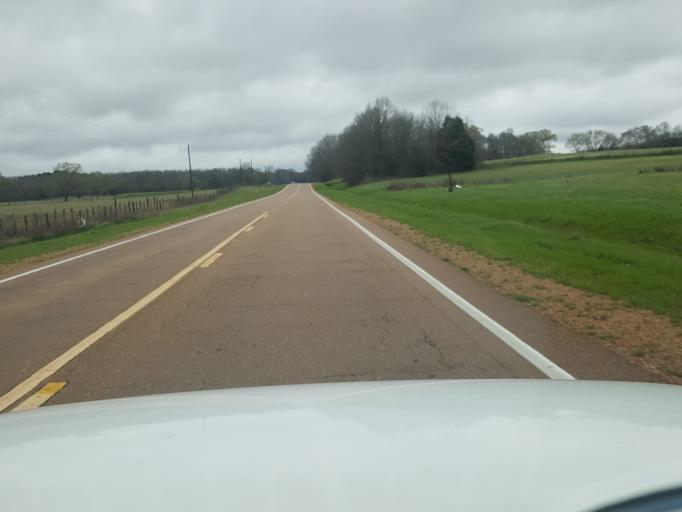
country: US
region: Mississippi
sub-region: Madison County
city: Canton
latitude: 32.7592
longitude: -90.1581
